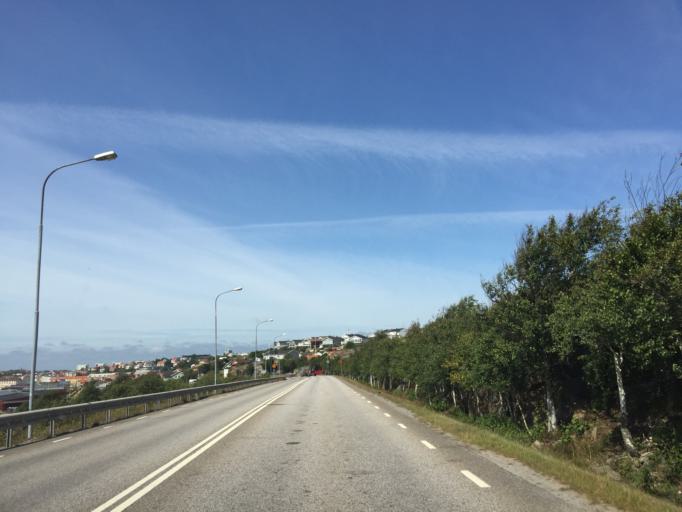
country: SE
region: Vaestra Goetaland
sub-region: Lysekils Kommun
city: Lysekil
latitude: 58.2779
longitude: 11.4585
